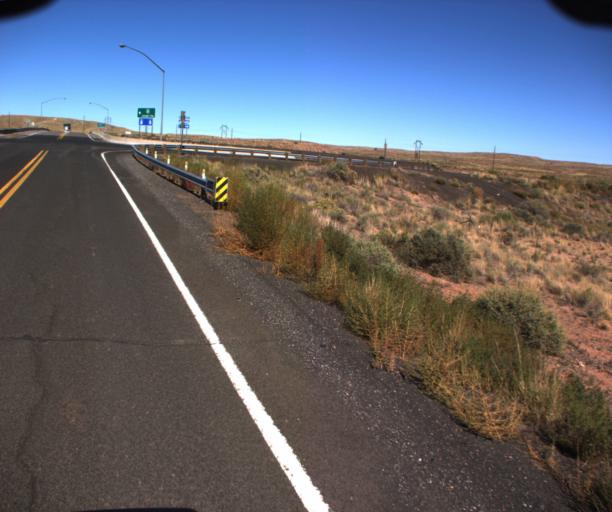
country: US
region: Arizona
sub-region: Navajo County
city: Joseph City
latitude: 34.9515
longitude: -110.3114
